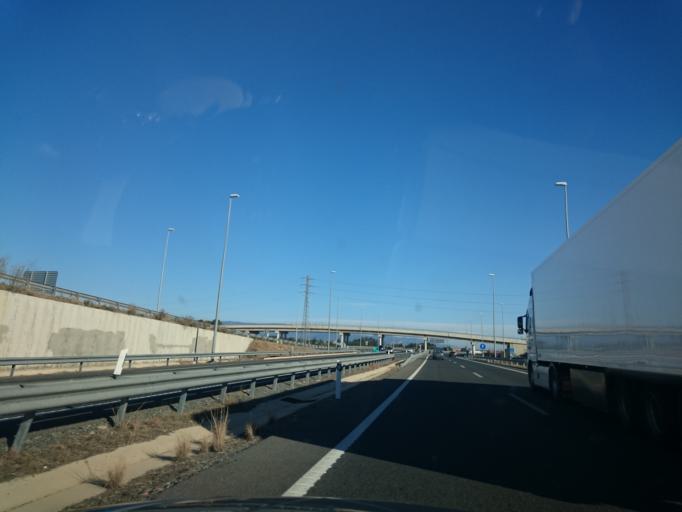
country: ES
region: Catalonia
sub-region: Provincia de Tarragona
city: Cambrils
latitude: 41.0581
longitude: 0.9905
